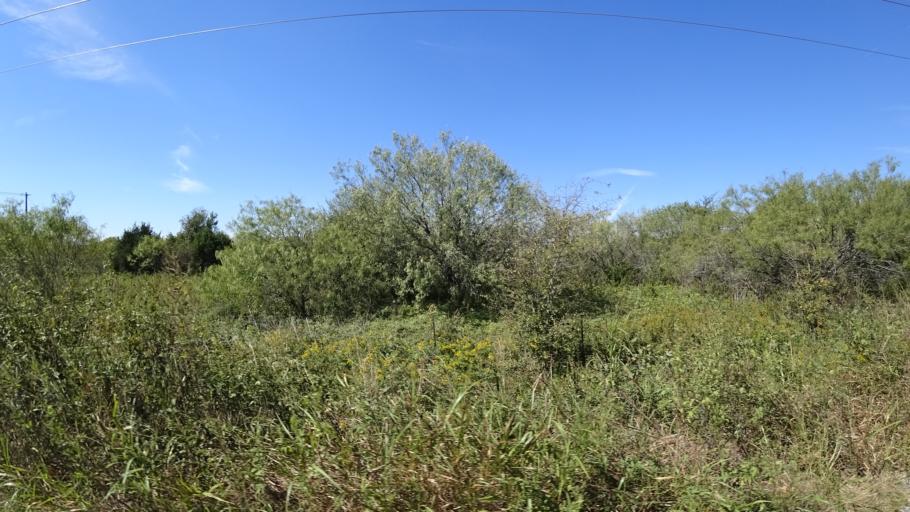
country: US
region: Texas
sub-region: Travis County
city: Austin
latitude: 30.1995
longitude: -97.6885
